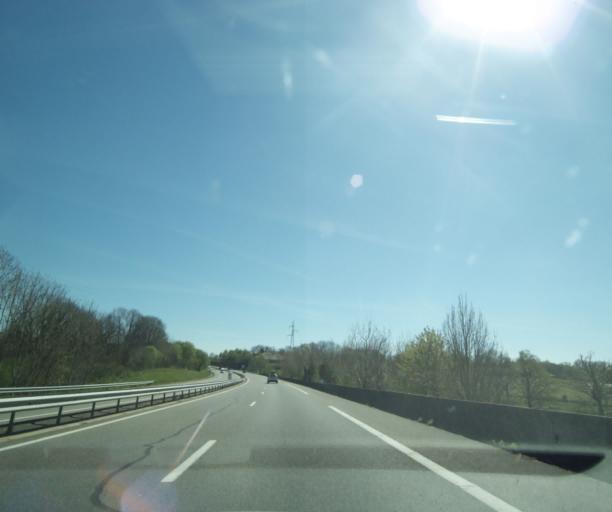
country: FR
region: Limousin
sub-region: Departement de la Correze
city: Uzerche
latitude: 45.5046
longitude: 1.5138
